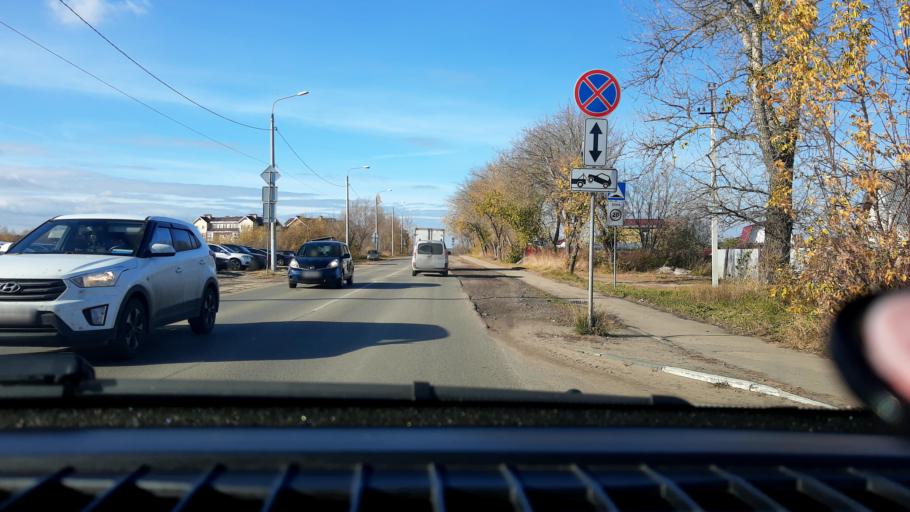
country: RU
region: Nizjnij Novgorod
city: Kstovo
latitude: 56.1627
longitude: 44.2006
